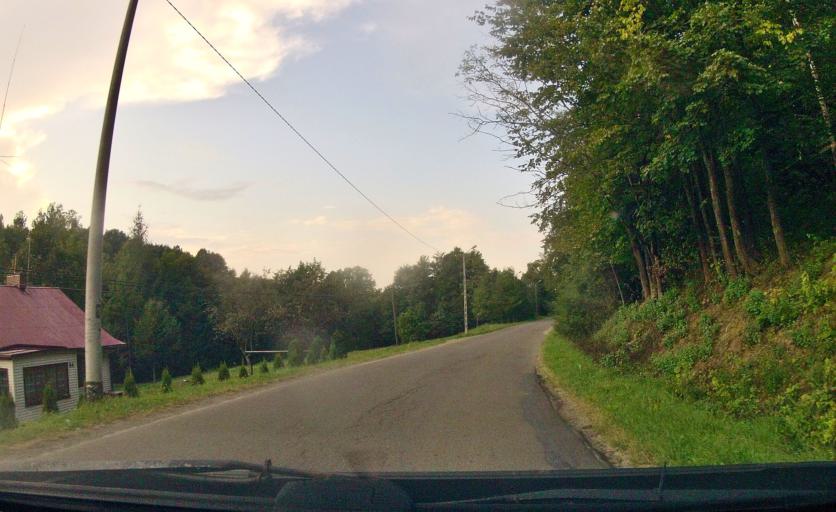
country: PL
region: Subcarpathian Voivodeship
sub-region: Powiat krosnienski
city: Dukla
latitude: 49.5506
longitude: 21.6222
